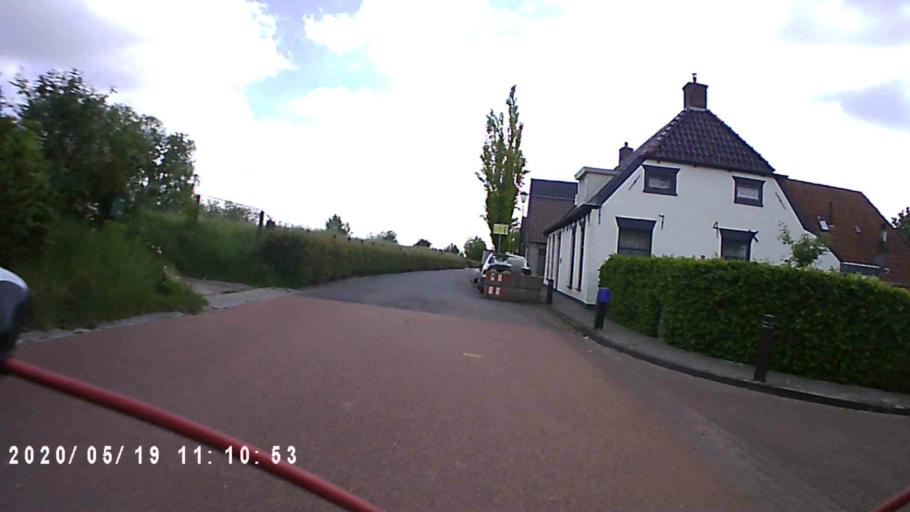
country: NL
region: Groningen
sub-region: Gemeente Zuidhorn
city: Grijpskerk
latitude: 53.2876
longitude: 6.3251
